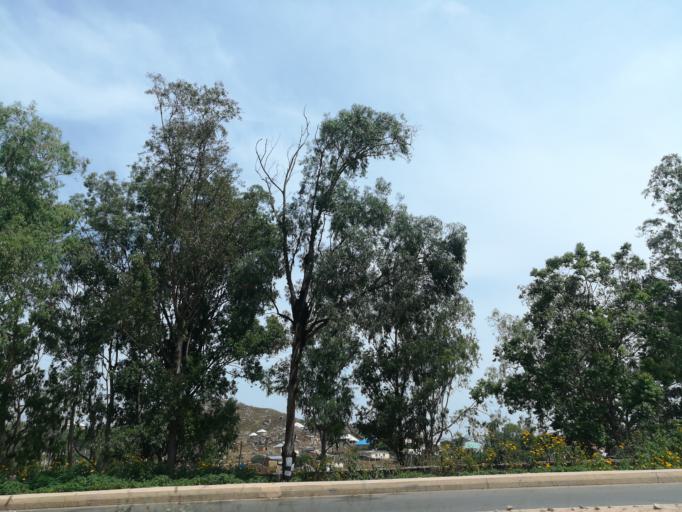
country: NG
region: Plateau
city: Bukuru
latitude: 9.8428
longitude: 8.8662
